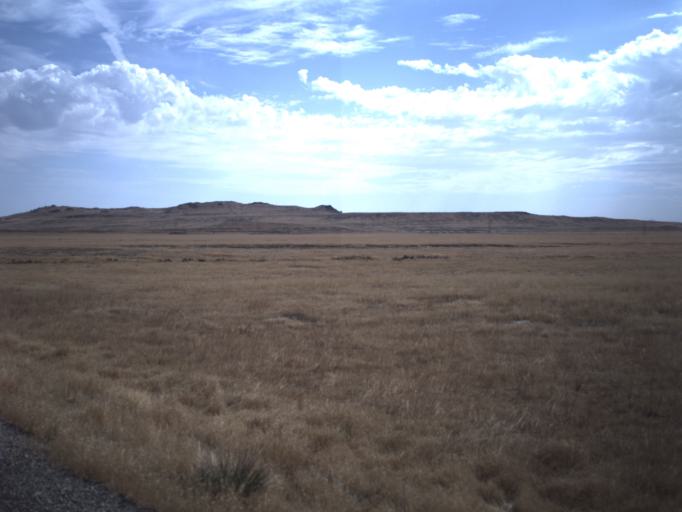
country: US
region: Utah
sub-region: Tooele County
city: Wendover
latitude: 41.3983
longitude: -113.9561
